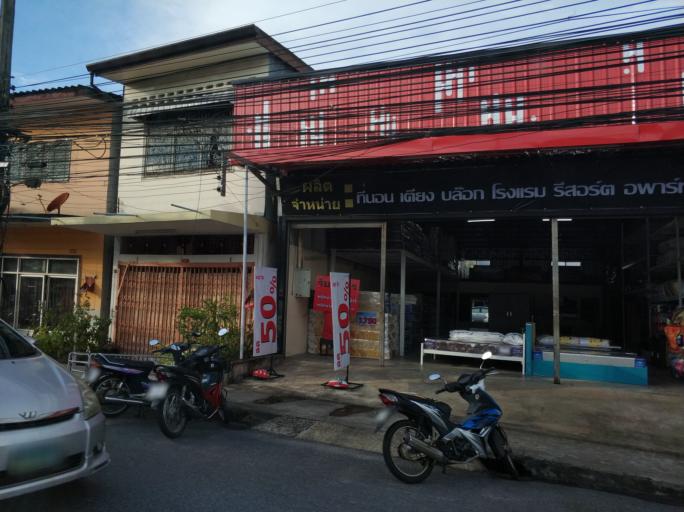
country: TH
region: Phuket
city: Wichit
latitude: 7.8867
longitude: 98.3747
